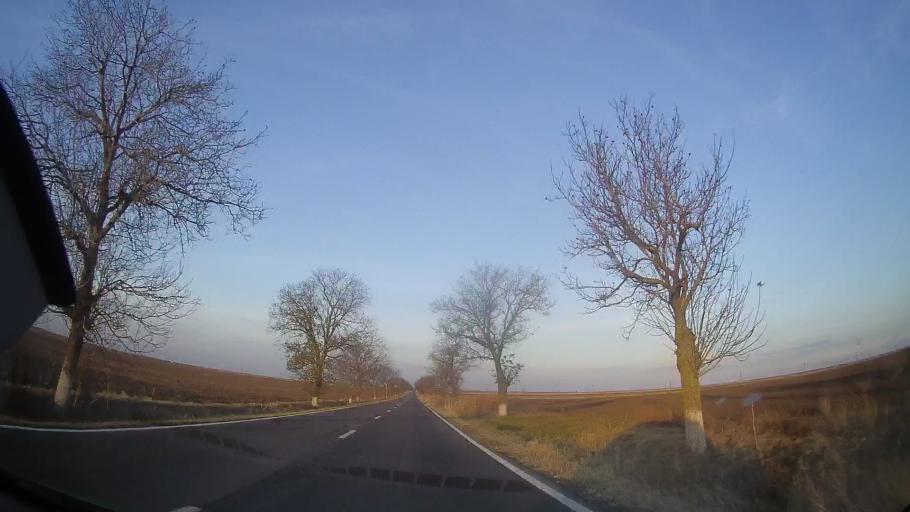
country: RO
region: Constanta
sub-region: Comuna Amzacea
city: Amzacea
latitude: 43.9803
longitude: 28.4148
